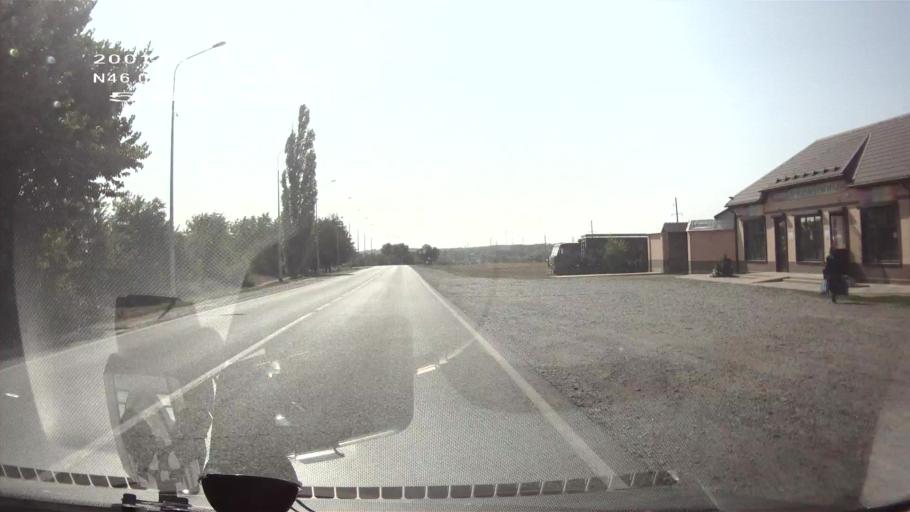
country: RU
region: Krasnodarskiy
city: Belaya Glina
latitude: 46.0878
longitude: 40.8309
